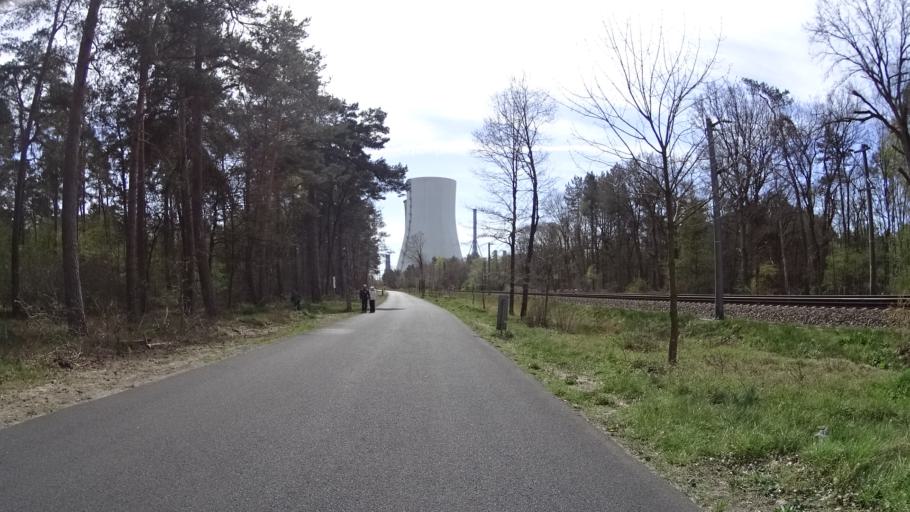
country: DE
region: Lower Saxony
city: Lingen
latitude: 52.4886
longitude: 7.3039
